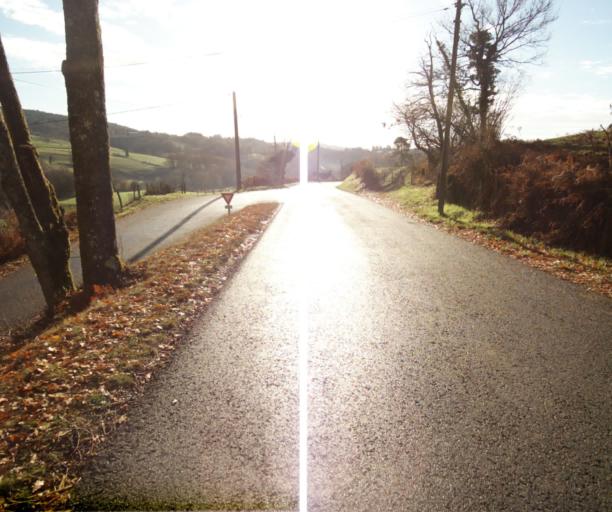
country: FR
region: Limousin
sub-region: Departement de la Correze
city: Saint-Mexant
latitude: 45.2394
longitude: 1.6385
